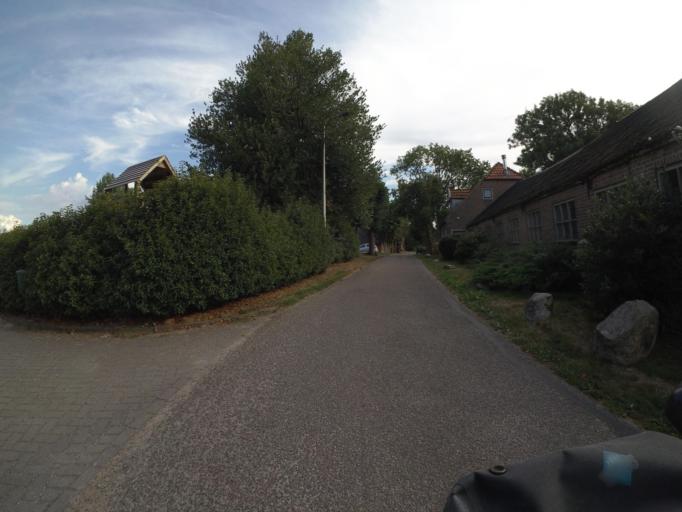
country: NL
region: Overijssel
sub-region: Gemeente Zwartewaterland
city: Hasselt
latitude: 52.6202
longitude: 6.1048
